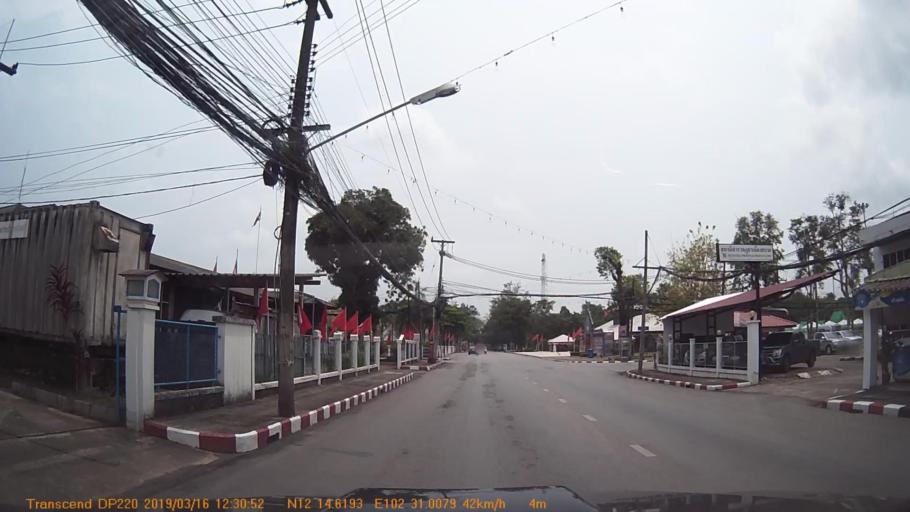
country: TH
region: Trat
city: Trat
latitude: 12.2436
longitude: 102.5168
